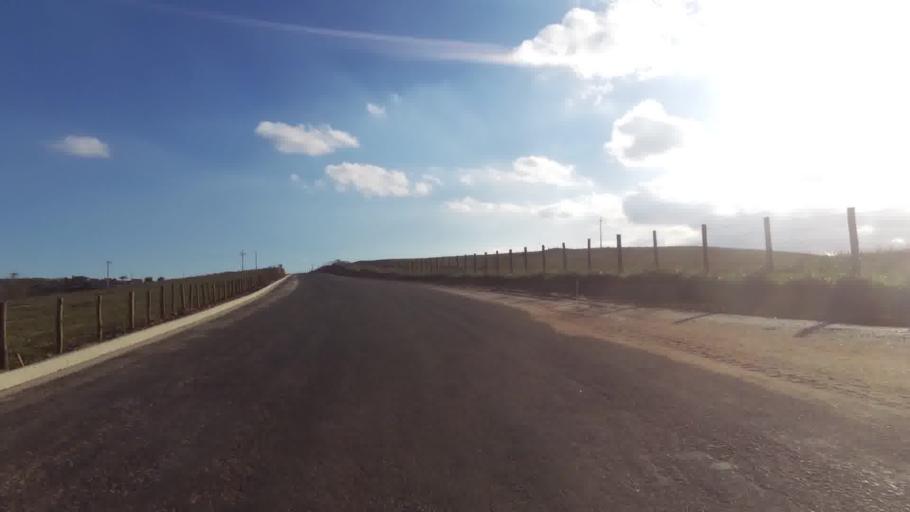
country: BR
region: Espirito Santo
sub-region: Marataizes
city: Marataizes
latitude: -21.1415
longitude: -41.0625
